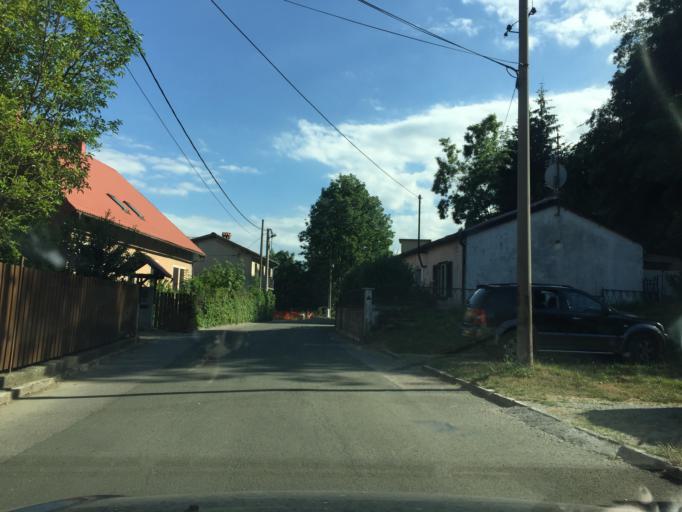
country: HR
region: Primorsko-Goranska
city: Klana
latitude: 45.4495
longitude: 14.3781
